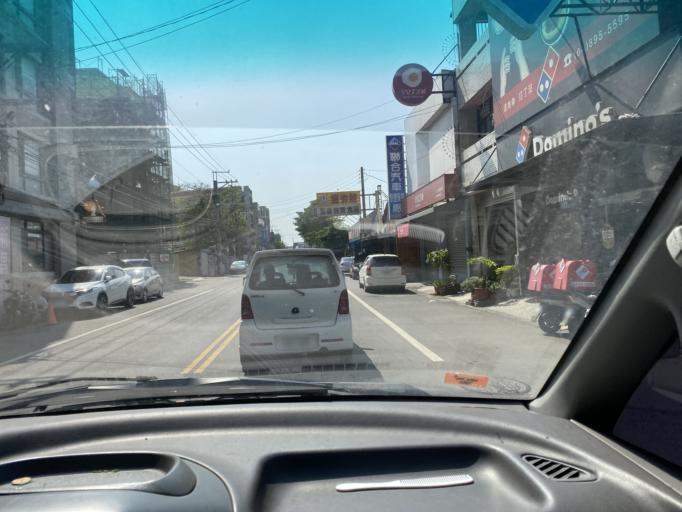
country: TW
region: Taiwan
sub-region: Changhua
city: Chang-hua
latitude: 23.9037
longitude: 120.3708
